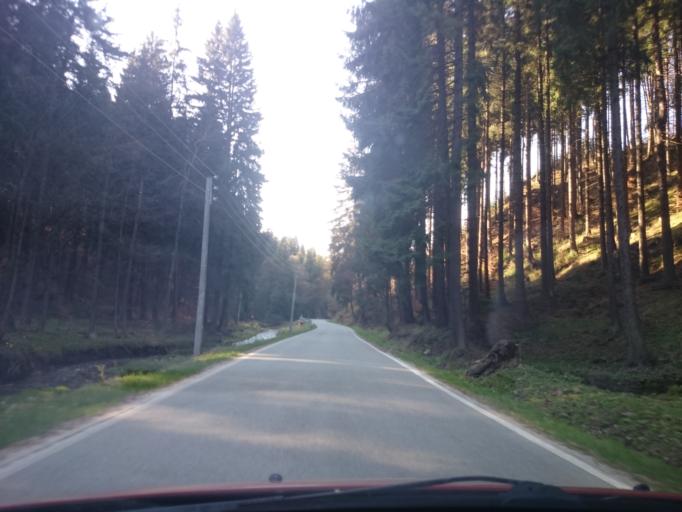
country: PL
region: Lower Silesian Voivodeship
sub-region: Powiat klodzki
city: Duszniki-Zdroj
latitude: 50.3485
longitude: 16.3997
